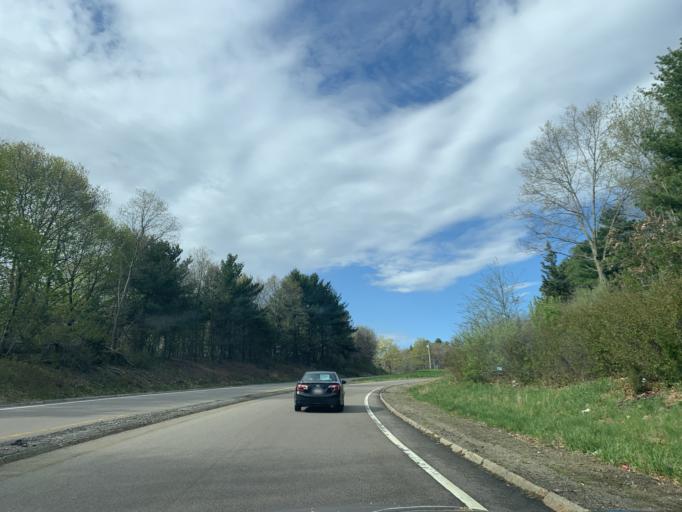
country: US
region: Massachusetts
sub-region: Norfolk County
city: Canton
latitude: 42.2020
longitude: -71.1173
